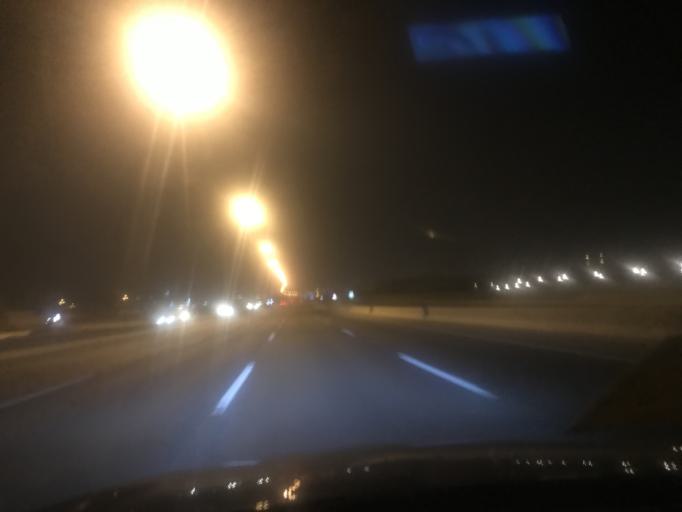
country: SA
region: Ar Riyad
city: Riyadh
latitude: 24.7716
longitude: 46.5739
